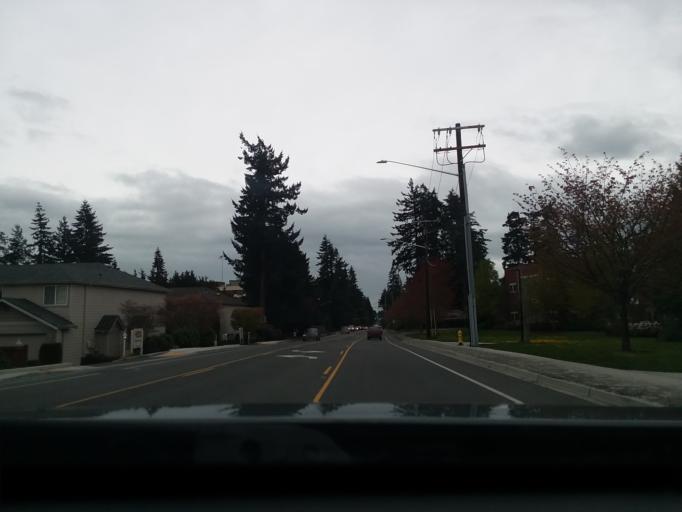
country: US
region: Washington
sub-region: Snohomish County
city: Lynnwood
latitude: 47.8061
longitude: -122.3358
